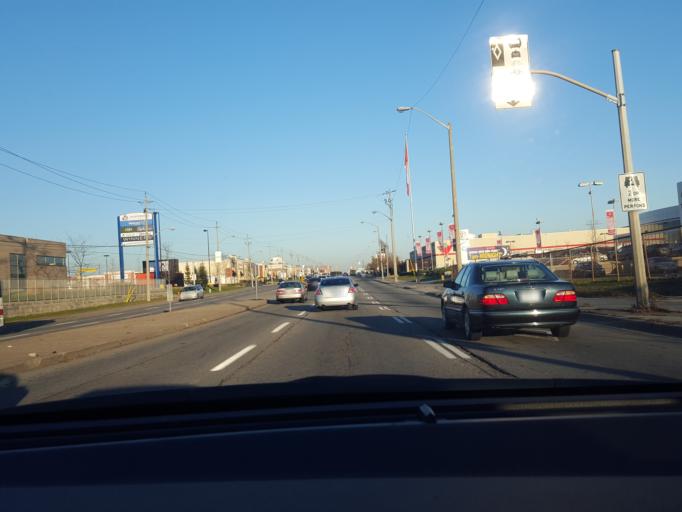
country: CA
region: Ontario
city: Scarborough
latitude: 43.7258
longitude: -79.2963
